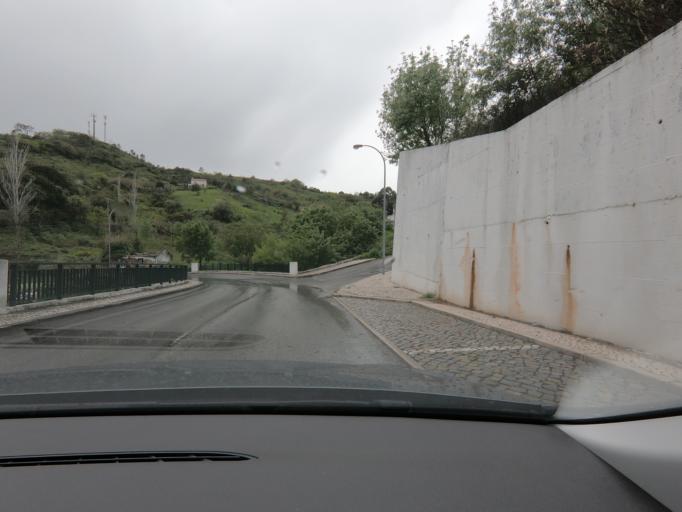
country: PT
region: Lisbon
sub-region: Alenquer
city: Alenquer
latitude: 39.0521
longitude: -9.0115
